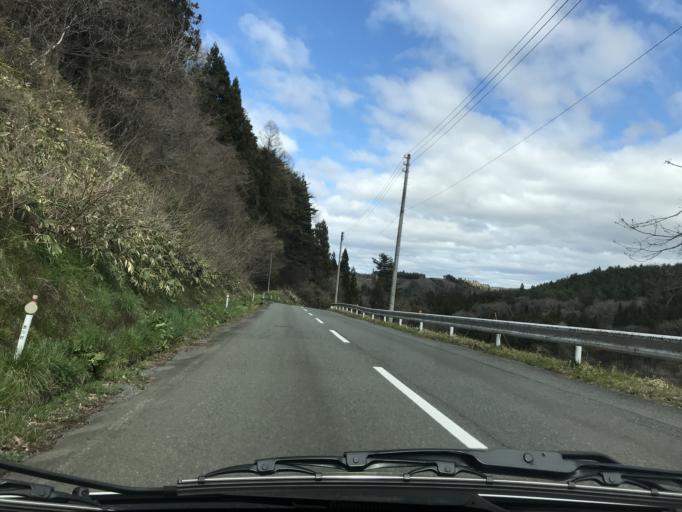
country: JP
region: Iwate
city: Mizusawa
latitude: 39.0758
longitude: 140.9941
